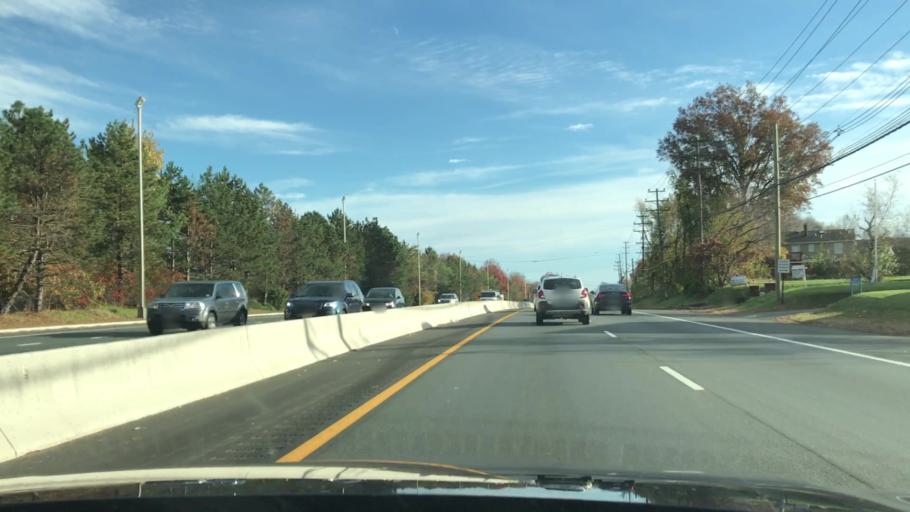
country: US
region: New Jersey
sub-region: Bergen County
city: Fair Lawn
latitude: 40.9417
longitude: -74.1288
